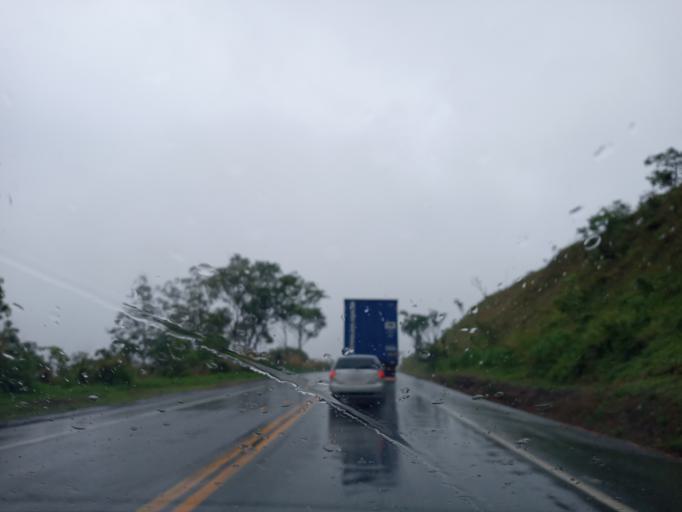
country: BR
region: Minas Gerais
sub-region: Luz
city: Luz
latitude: -19.7151
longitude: -45.8841
